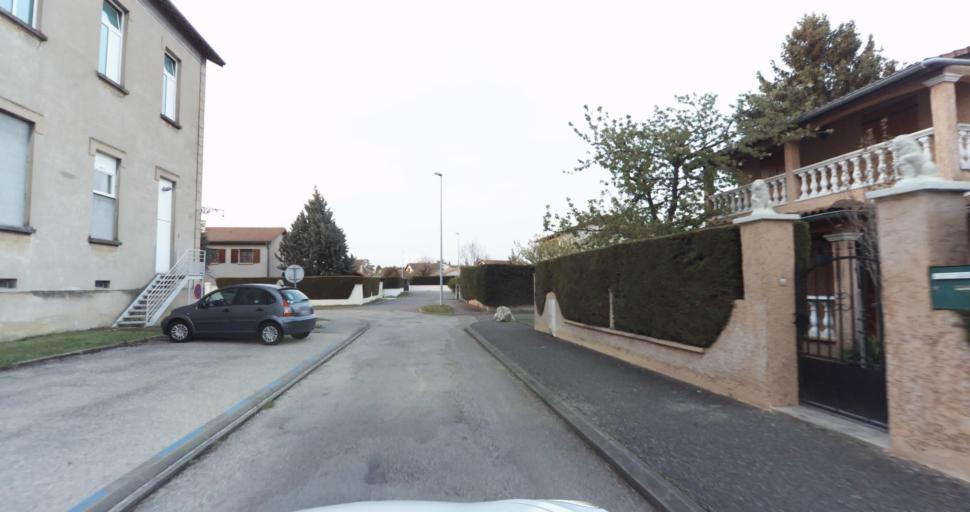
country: FR
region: Rhone-Alpes
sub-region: Departement de l'Ain
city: Amberieu-en-Bugey
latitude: 45.9559
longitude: 5.3374
